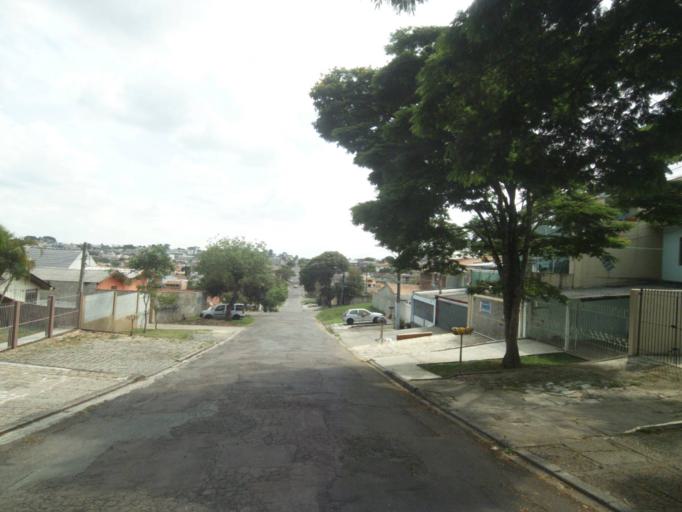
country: BR
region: Parana
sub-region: Pinhais
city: Pinhais
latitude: -25.4014
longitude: -49.2018
